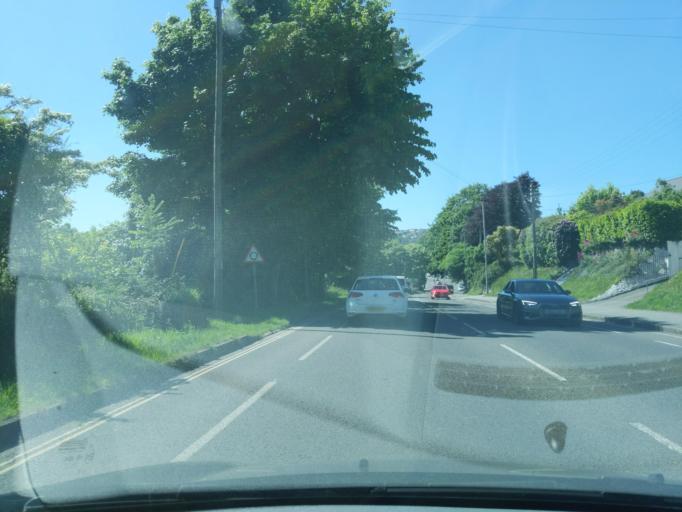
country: GB
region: England
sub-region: Cornwall
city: St Austell
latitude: 50.3337
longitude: -4.7908
